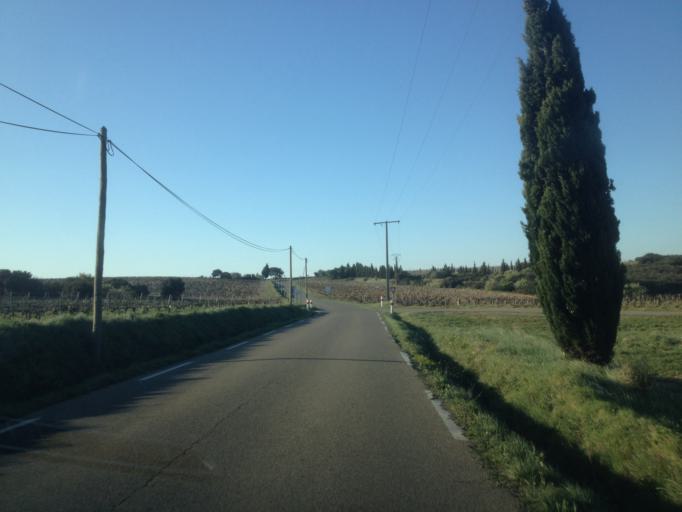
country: FR
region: Provence-Alpes-Cote d'Azur
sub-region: Departement du Vaucluse
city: Chateauneuf-du-Pape
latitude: 44.0749
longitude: 4.8329
